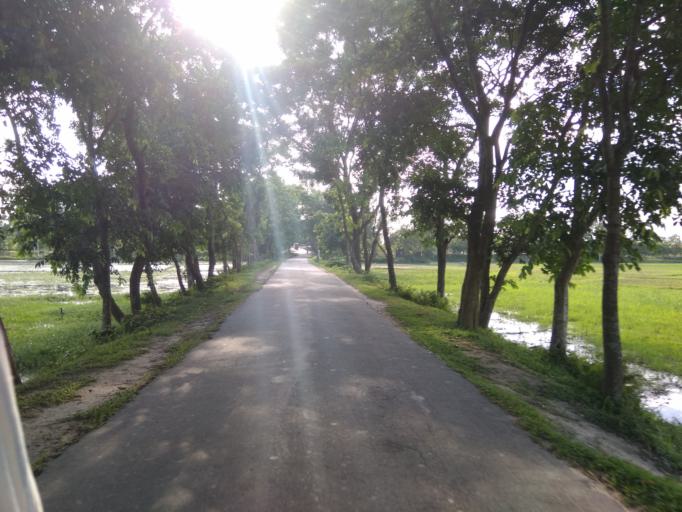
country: BD
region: Rangpur Division
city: Rangpur
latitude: 25.8317
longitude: 89.1153
